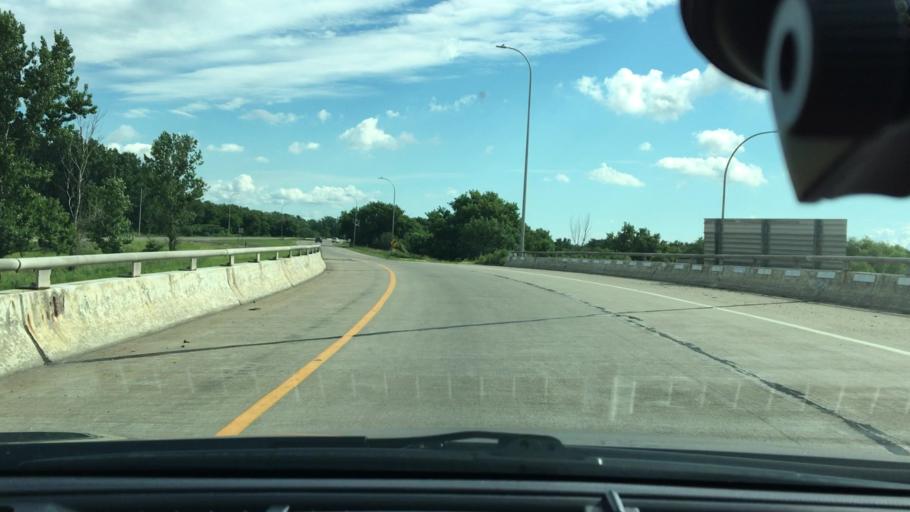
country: US
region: Minnesota
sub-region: Hennepin County
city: Wayzata
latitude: 44.9750
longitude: -93.5305
